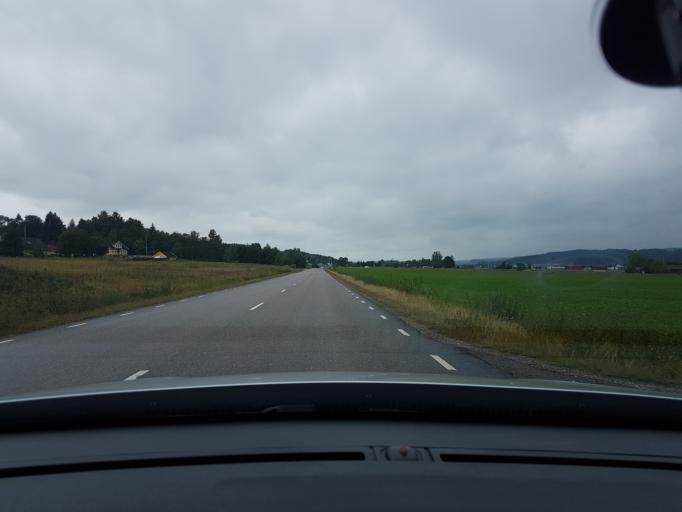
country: SE
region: Vaestra Goetaland
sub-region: Ale Kommun
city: Alvangen
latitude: 57.9689
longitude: 12.1587
